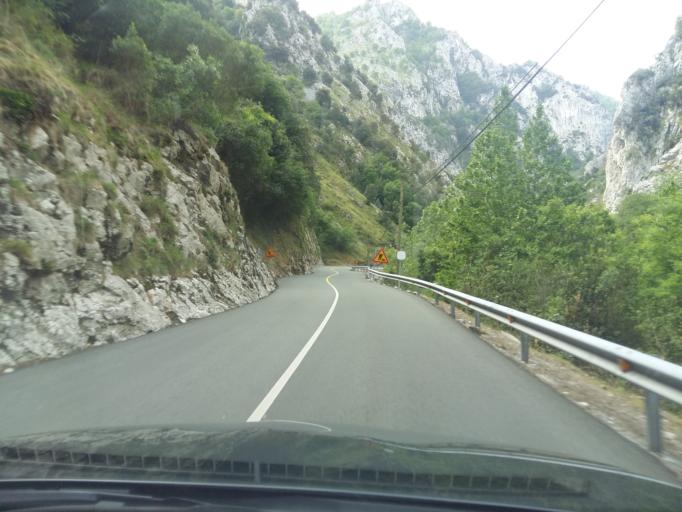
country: ES
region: Cantabria
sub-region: Provincia de Cantabria
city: Tresviso
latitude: 43.3016
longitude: -4.6063
